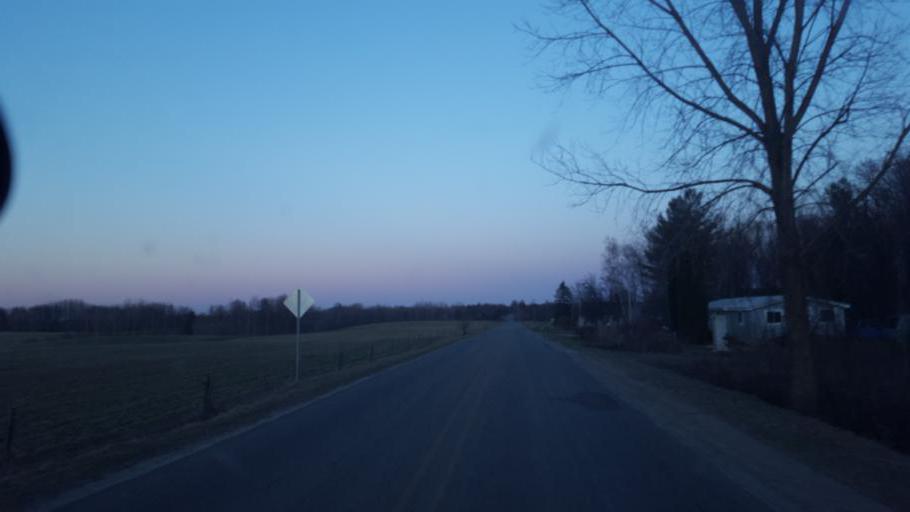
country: US
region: Michigan
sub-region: Montcalm County
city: Howard City
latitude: 43.5259
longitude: -85.4802
